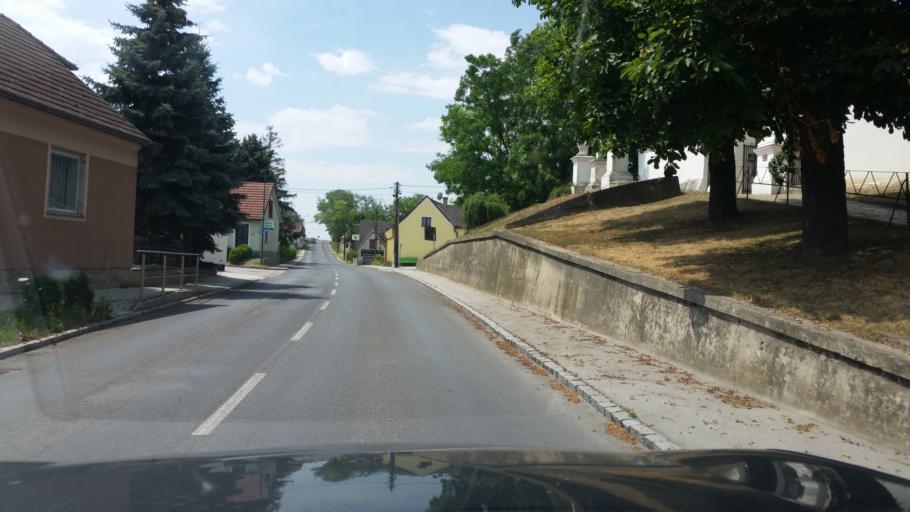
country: AT
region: Lower Austria
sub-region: Politischer Bezirk Mistelbach
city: Hausbrunn
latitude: 48.5902
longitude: 16.8157
